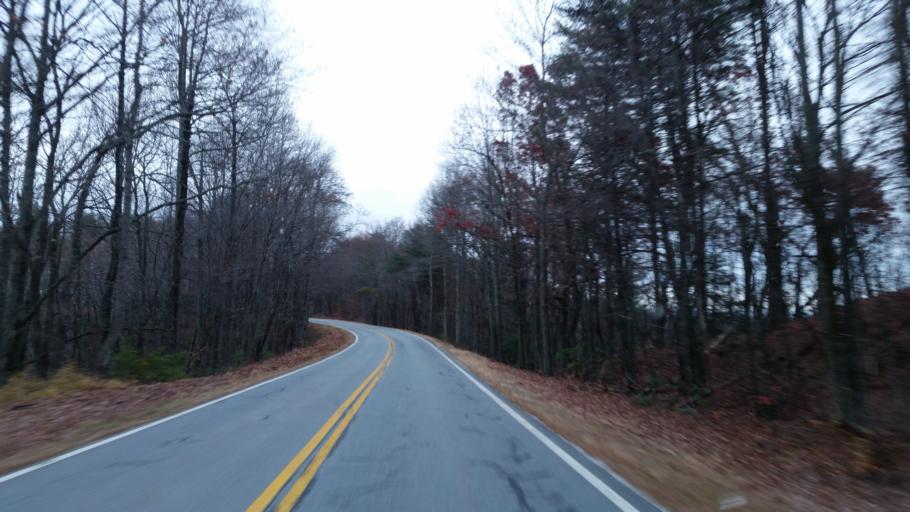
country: US
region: Georgia
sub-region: Pickens County
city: Jasper
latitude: 34.5352
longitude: -84.3069
